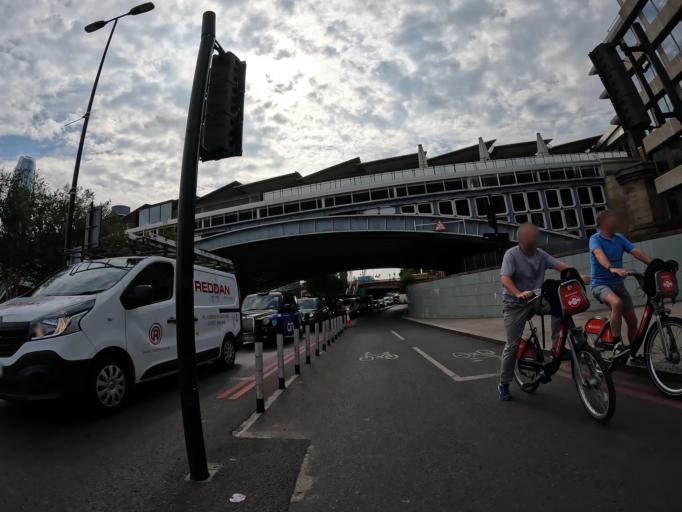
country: GB
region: England
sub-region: Greater London
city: Islington
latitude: 51.5453
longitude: -0.0847
